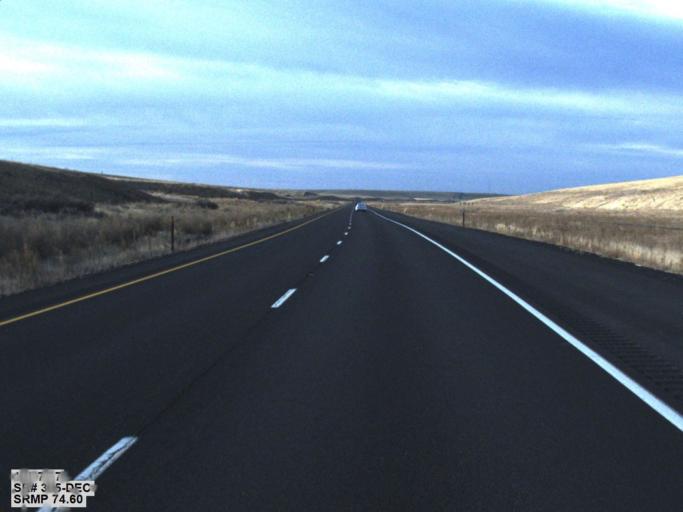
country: US
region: Washington
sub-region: Franklin County
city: Connell
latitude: 46.8705
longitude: -118.6306
